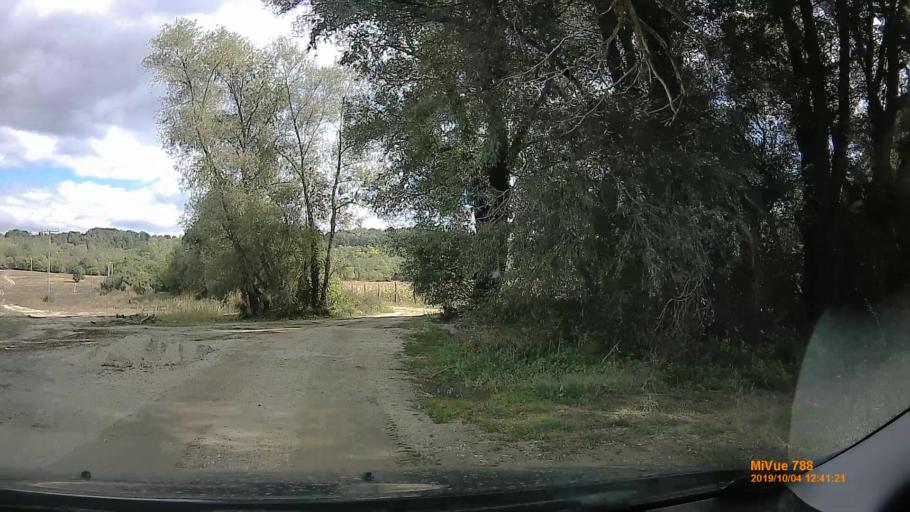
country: HU
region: Somogy
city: Karad
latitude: 46.6809
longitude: 17.7782
